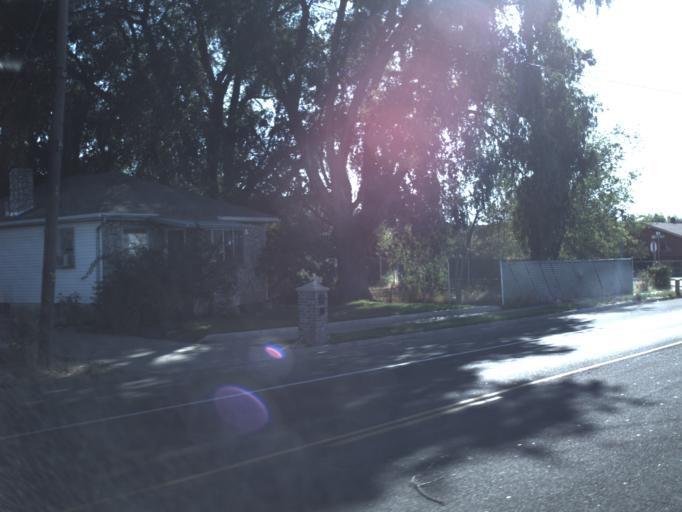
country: US
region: Utah
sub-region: Davis County
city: Clinton
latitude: 41.1399
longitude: -112.0692
